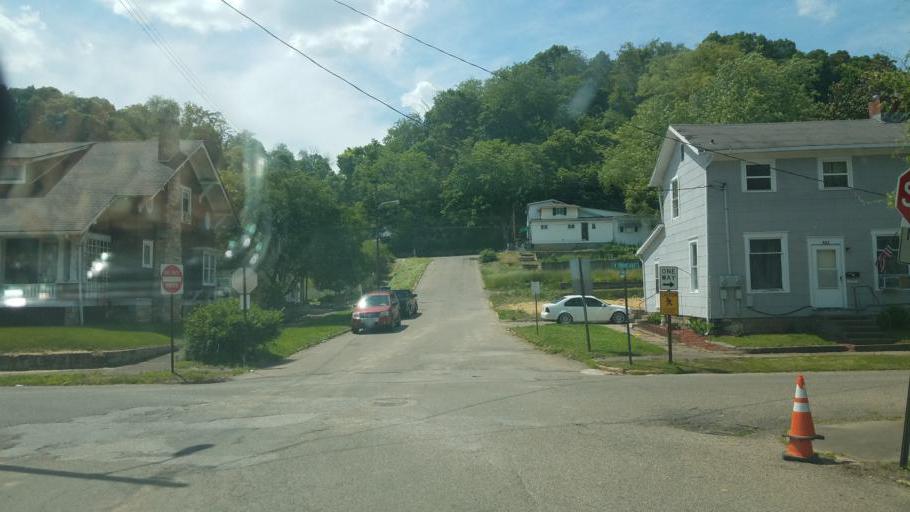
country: US
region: Ohio
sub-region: Meigs County
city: Middleport
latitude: 39.0042
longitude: -82.0482
